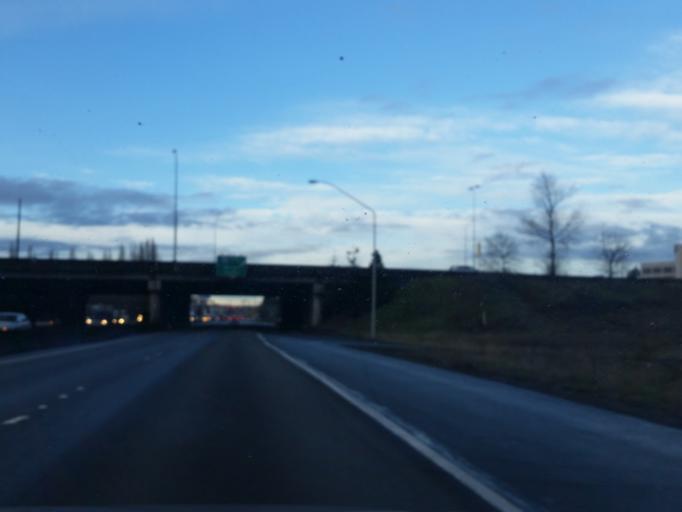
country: US
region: Washington
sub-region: King County
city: Renton
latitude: 47.4669
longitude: -122.2179
